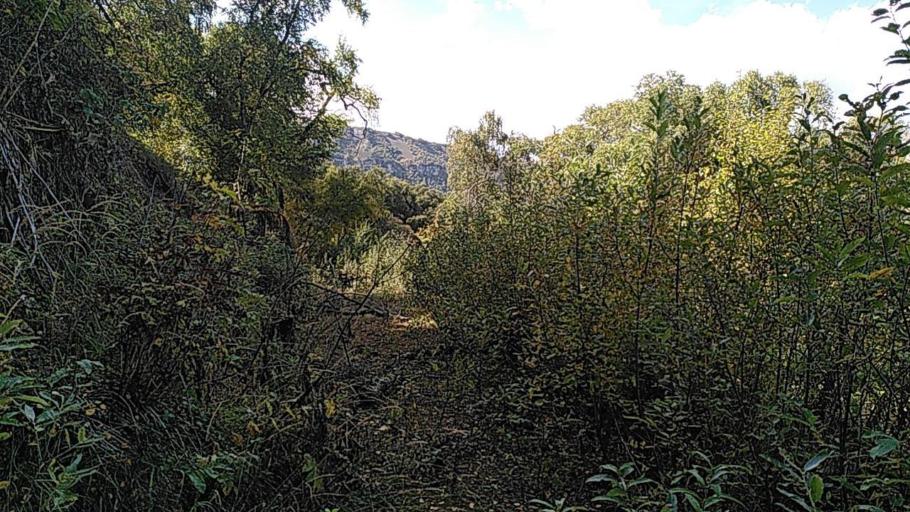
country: RU
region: Kabardino-Balkariya
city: Kamennomostskoye
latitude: 43.6716
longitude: 42.8151
